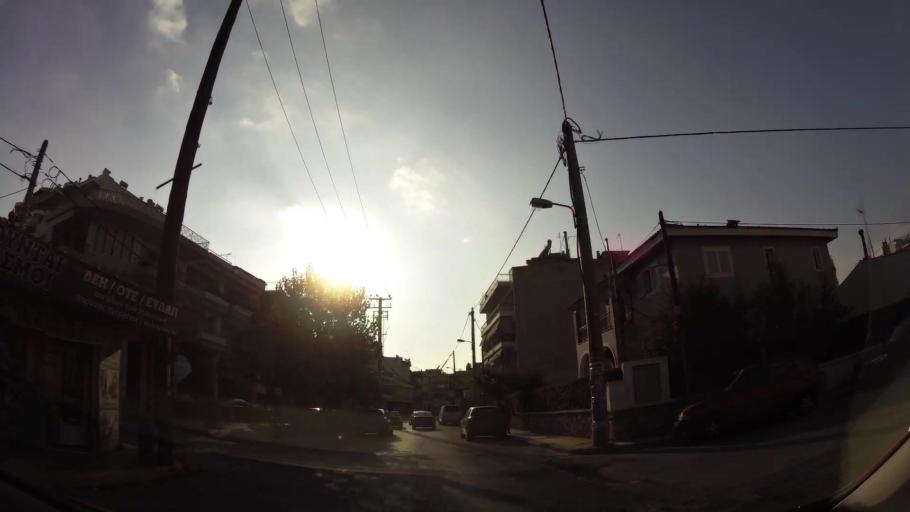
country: GR
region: Attica
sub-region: Nomarchia Anatolikis Attikis
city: Acharnes
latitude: 38.0822
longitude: 23.7411
